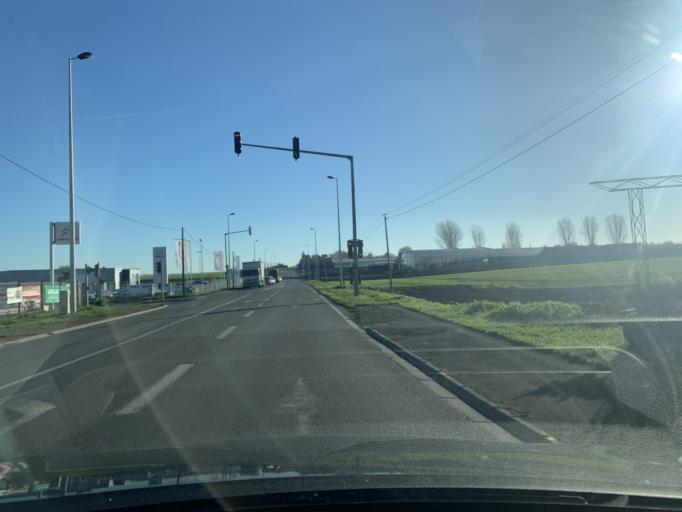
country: FR
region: Nord-Pas-de-Calais
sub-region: Departement du Nord
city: Escaudoeuvres
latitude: 50.1669
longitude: 3.2684
